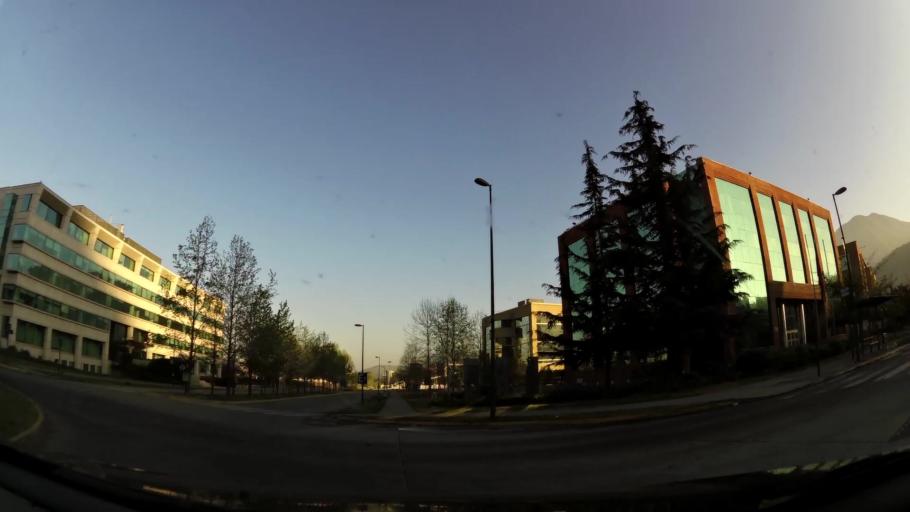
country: CL
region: Santiago Metropolitan
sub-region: Provincia de Santiago
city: Santiago
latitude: -33.3930
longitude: -70.6146
